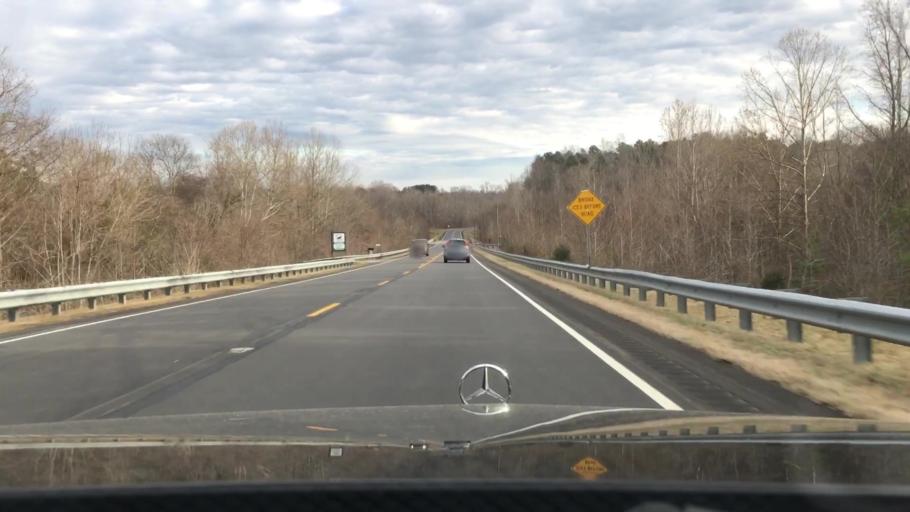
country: US
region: North Carolina
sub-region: Caswell County
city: Yanceyville
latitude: 36.3206
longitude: -79.2280
